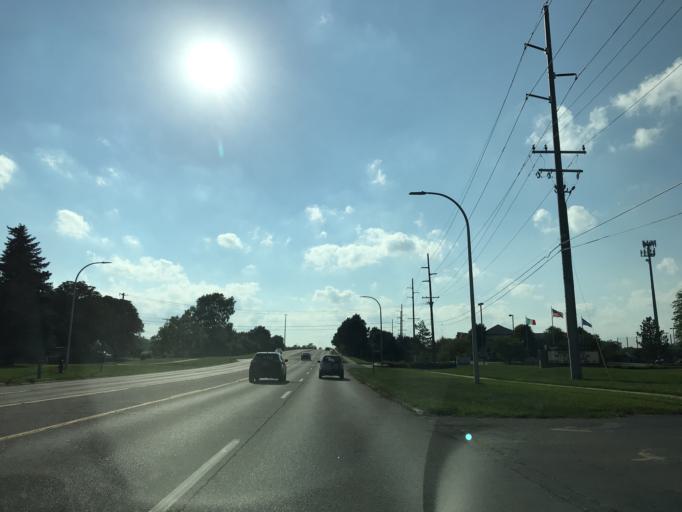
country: US
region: Michigan
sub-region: Wayne County
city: Plymouth
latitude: 42.3961
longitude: -83.4269
